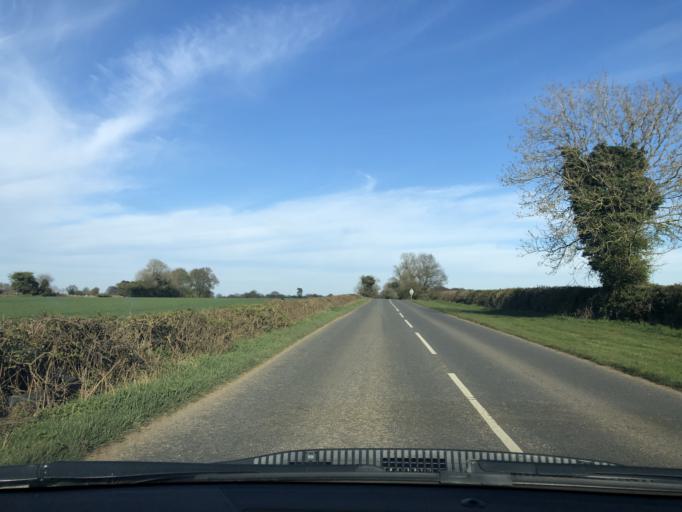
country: GB
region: England
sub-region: Oxfordshire
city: Hook Norton
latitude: 52.0130
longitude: -1.4507
